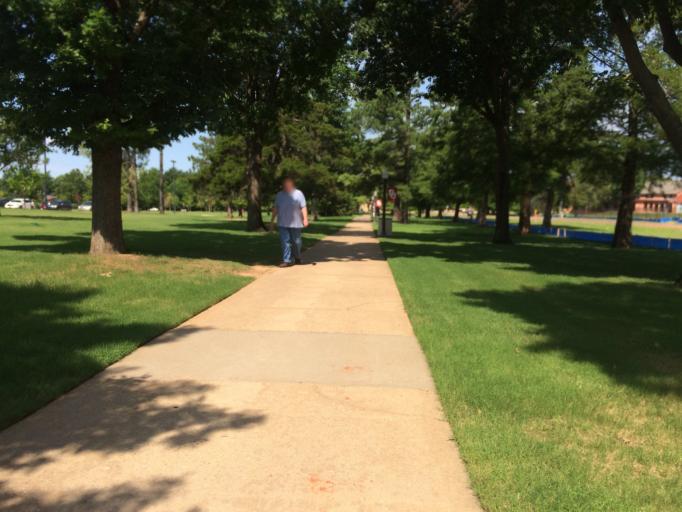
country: US
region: Oklahoma
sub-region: Cleveland County
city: Norman
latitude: 35.1964
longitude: -97.4471
